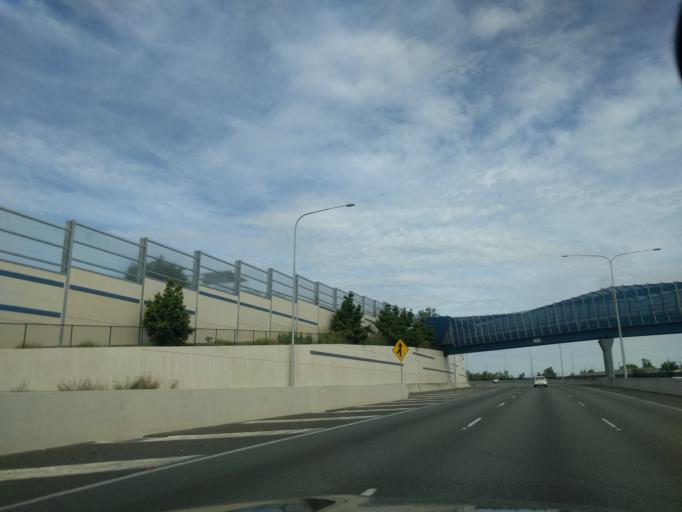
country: AU
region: Queensland
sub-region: Ipswich
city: Goodna
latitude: -27.6066
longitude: 152.8956
